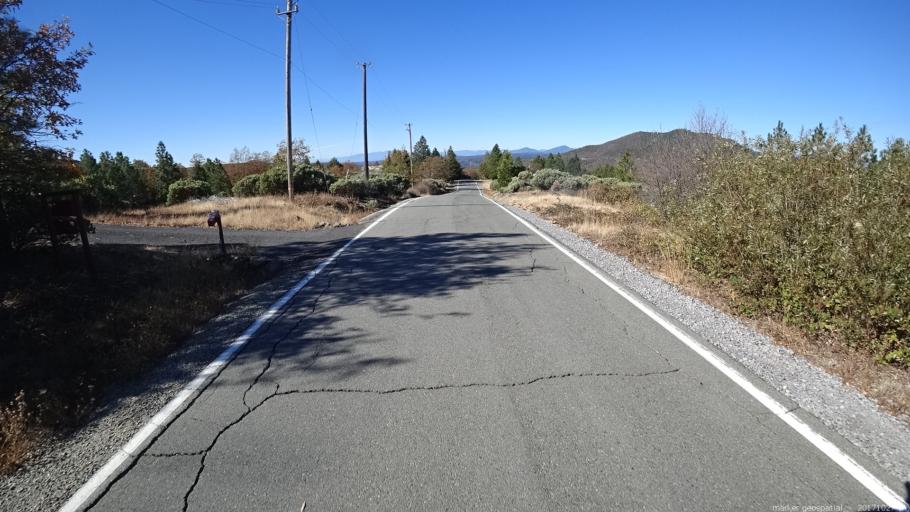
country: US
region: California
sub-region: Shasta County
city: Burney
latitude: 40.7907
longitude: -121.9179
